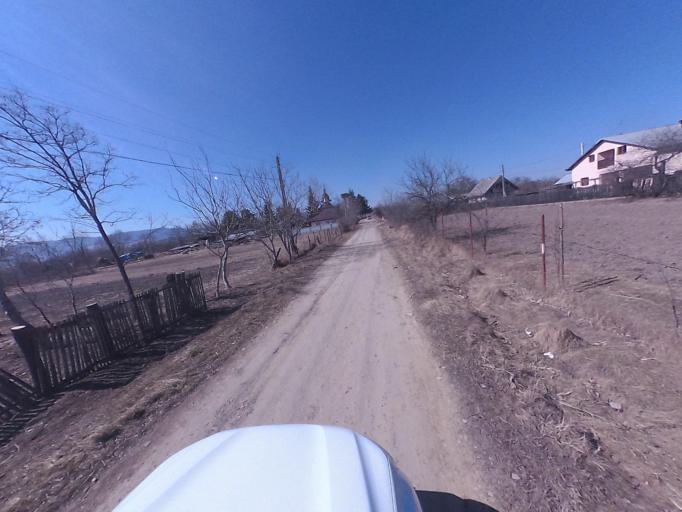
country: RO
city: Vanatori-Neamt
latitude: 47.1825
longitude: 26.3295
